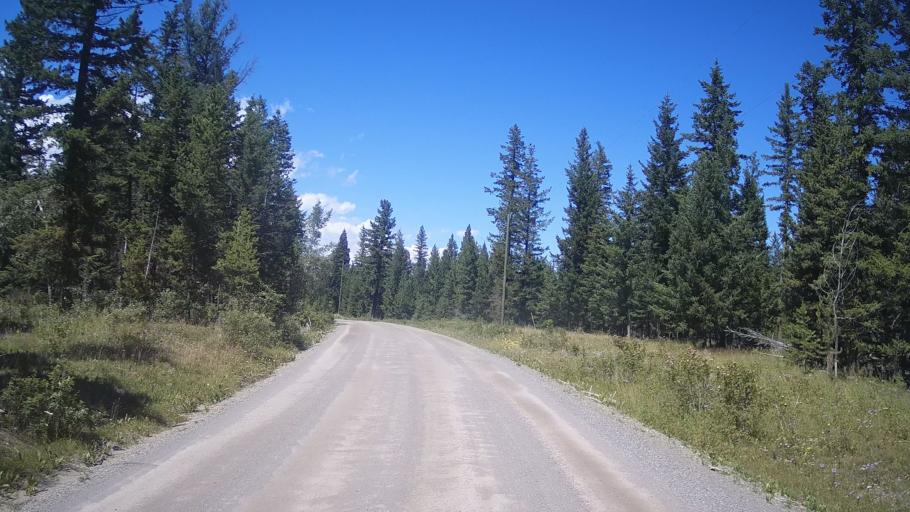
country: CA
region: British Columbia
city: Cache Creek
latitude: 51.1910
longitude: -121.5862
